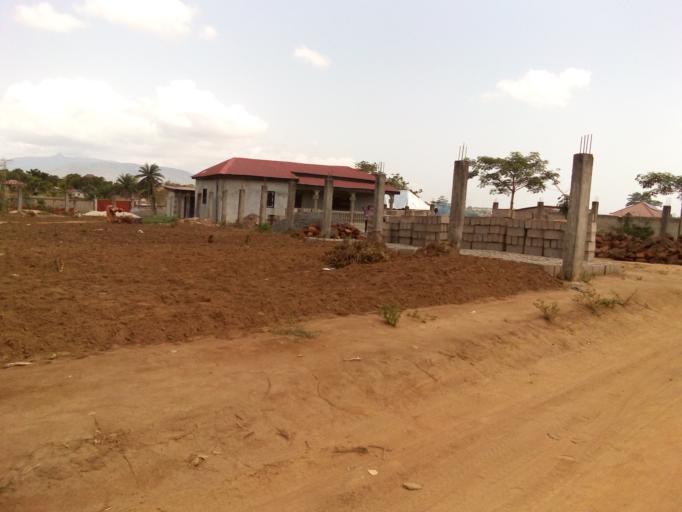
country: SL
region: Western Area
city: Waterloo
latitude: 8.3379
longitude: -13.0197
